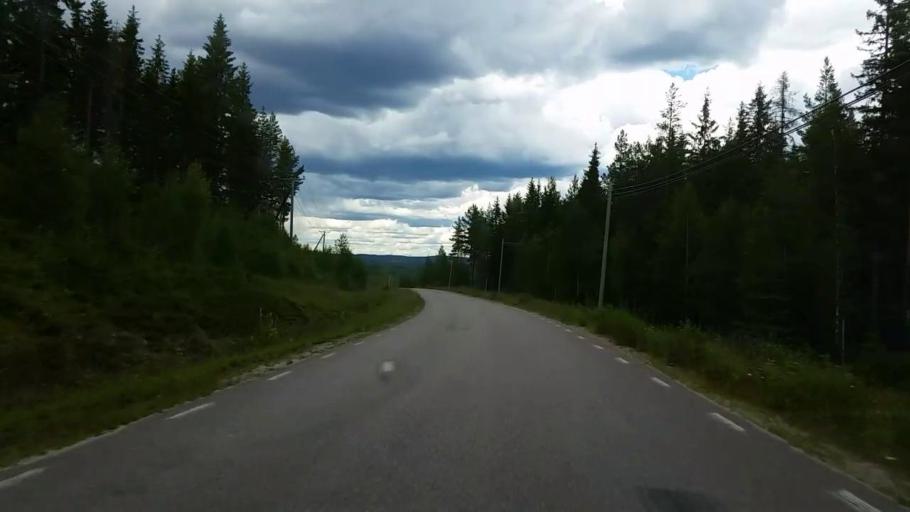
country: SE
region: Gaevleborg
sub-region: Ovanakers Kommun
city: Edsbyn
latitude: 61.4319
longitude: 15.8988
